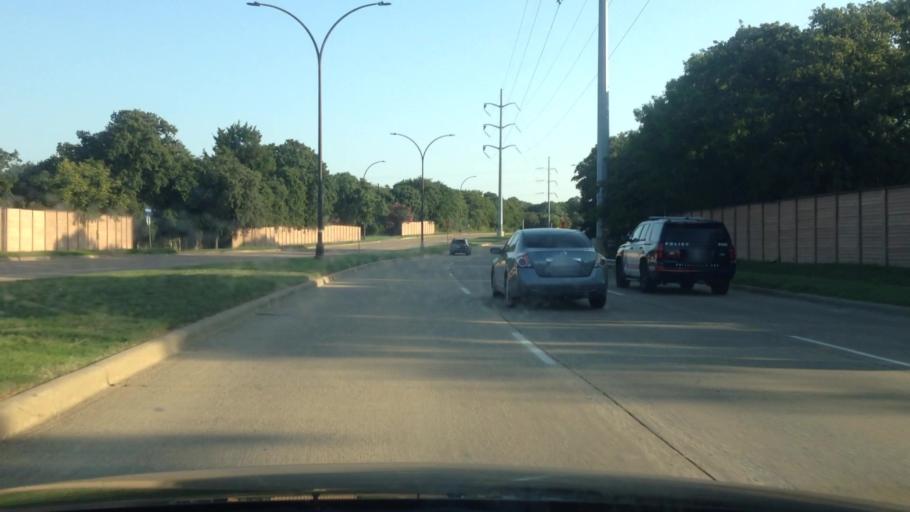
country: US
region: Texas
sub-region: Tarrant County
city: Dalworthington Gardens
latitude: 32.6928
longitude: -97.1904
